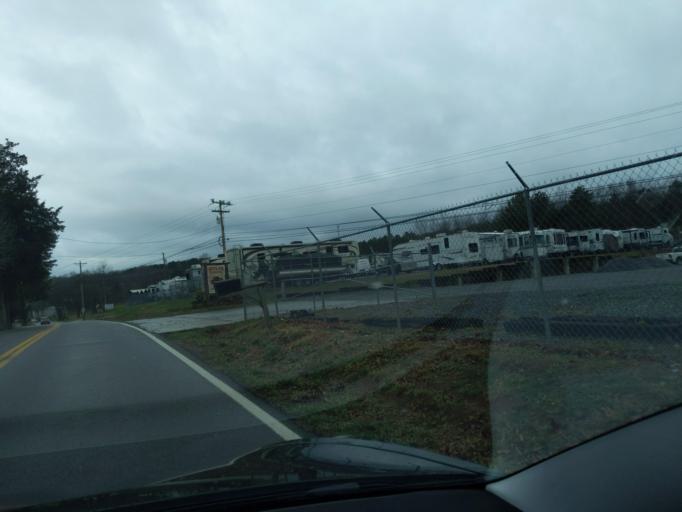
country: US
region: Tennessee
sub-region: Sevier County
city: Sevierville
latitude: 35.9728
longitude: -83.5382
